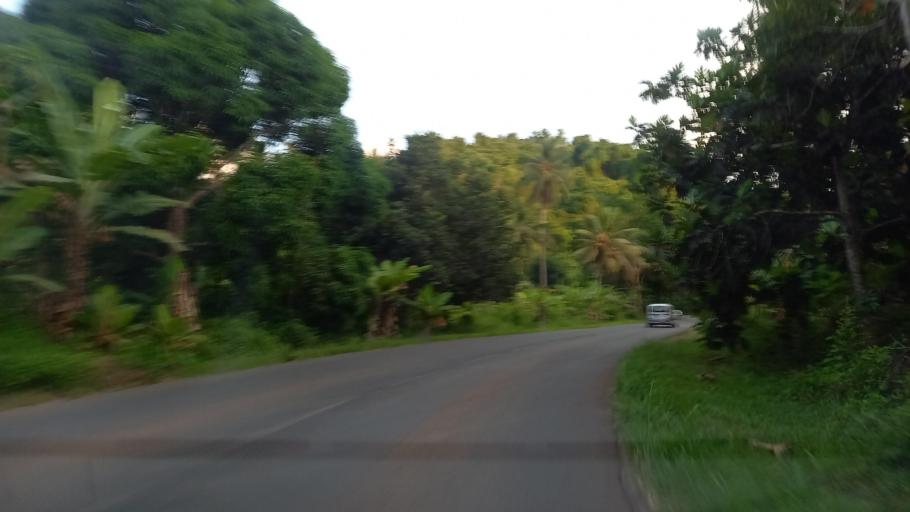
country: YT
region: M'Tsangamouji
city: M'Tsangamouji
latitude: -12.7613
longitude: 45.1033
